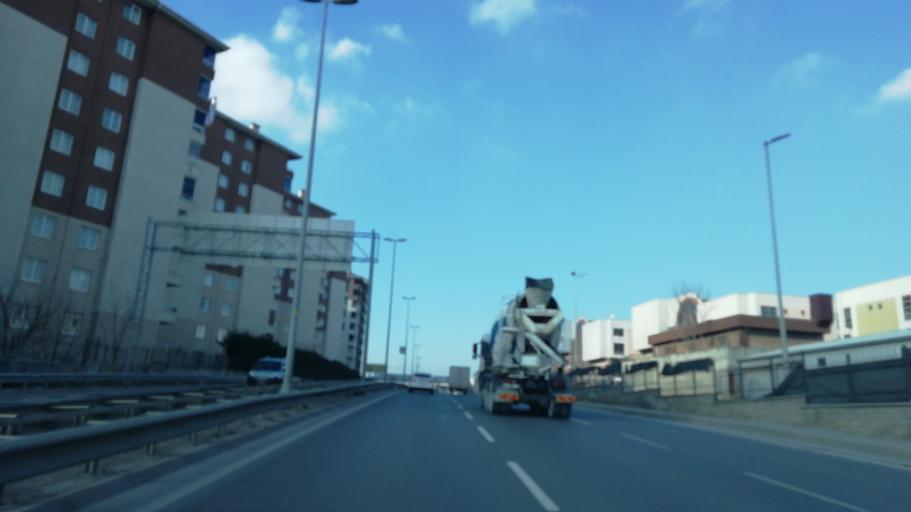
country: TR
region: Istanbul
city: Esenler
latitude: 41.0648
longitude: 28.8663
